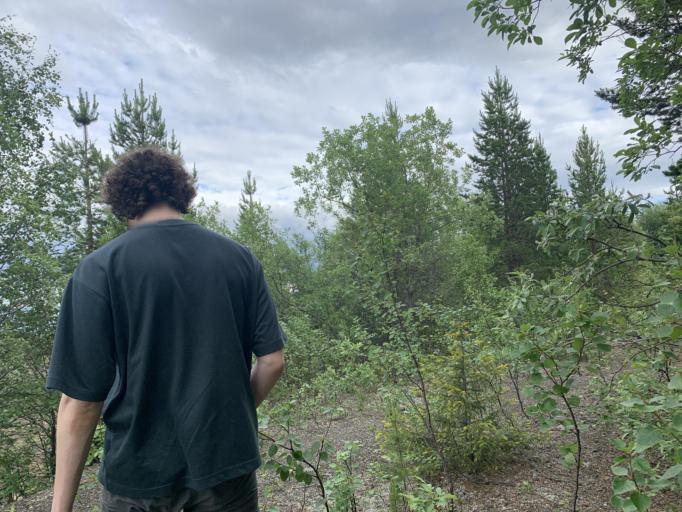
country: RU
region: Murmansk
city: Monchegorsk
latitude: 67.8766
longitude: 33.0813
